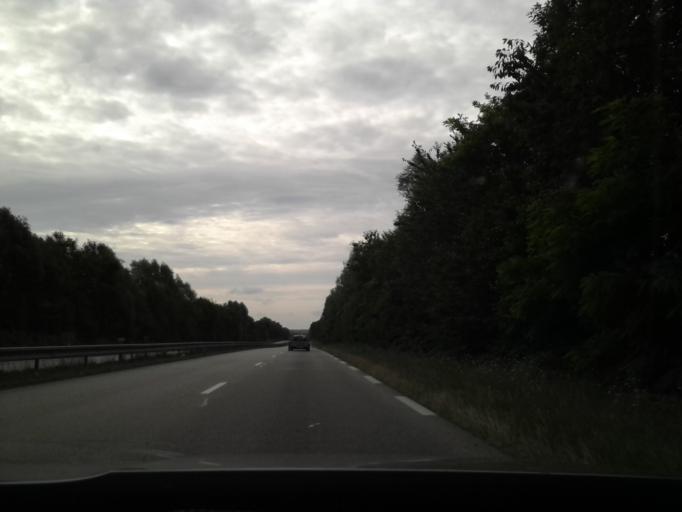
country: FR
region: Lower Normandy
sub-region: Departement de la Manche
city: Montebourg
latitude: 49.4903
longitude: -1.4040
